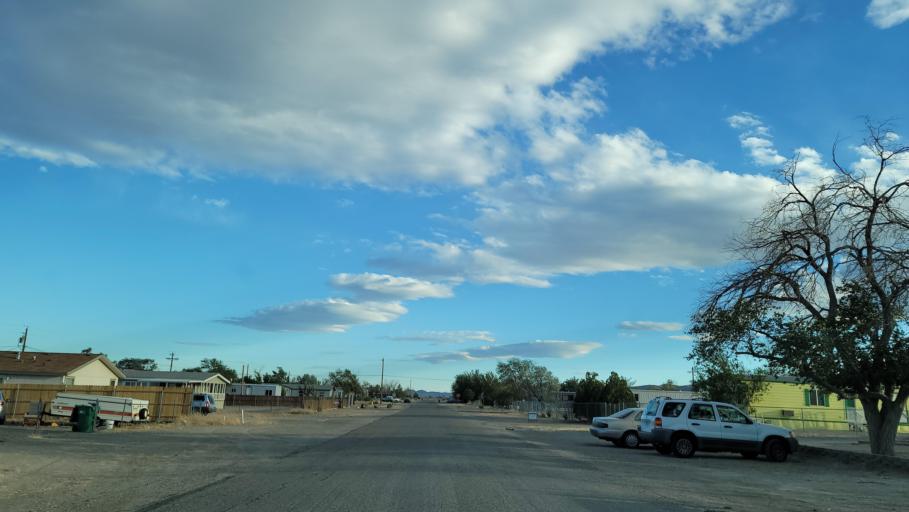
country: US
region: Nevada
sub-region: Lyon County
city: Silver Springs
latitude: 39.4084
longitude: -119.2222
